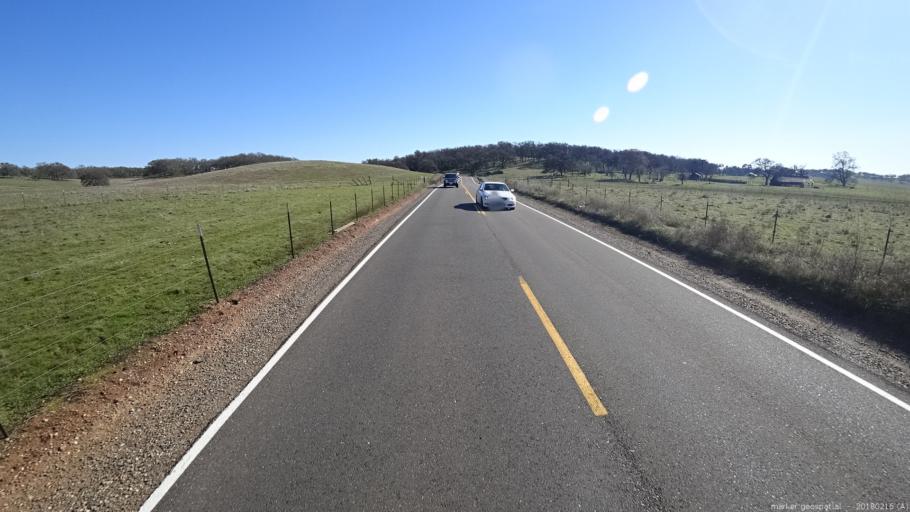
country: US
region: California
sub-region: Sacramento County
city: Rancho Murieta
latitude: 38.5453
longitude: -121.1108
